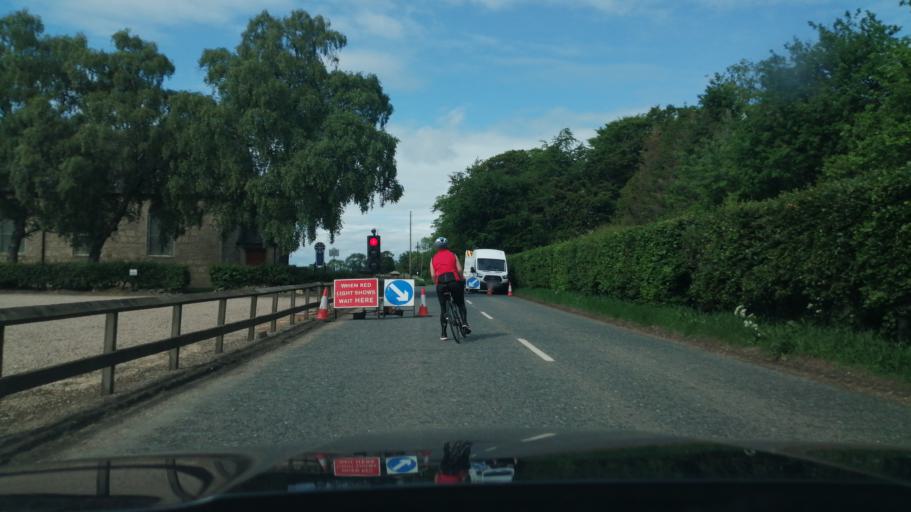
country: GB
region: Scotland
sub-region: Moray
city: Lhanbryd
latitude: 57.6422
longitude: -3.2475
